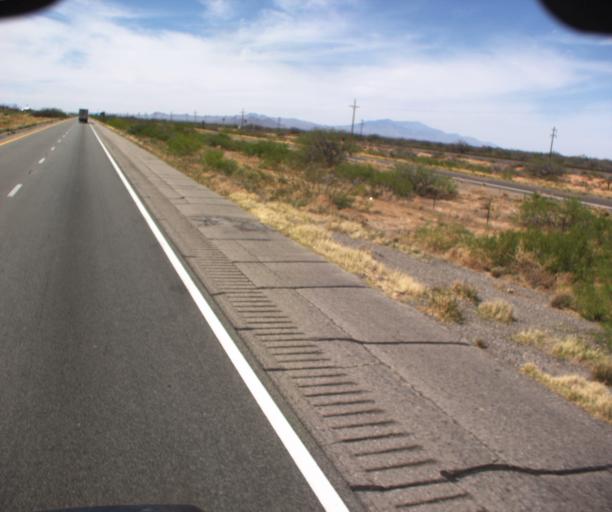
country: US
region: Arizona
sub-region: Cochise County
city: Willcox
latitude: 32.3134
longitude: -109.4235
